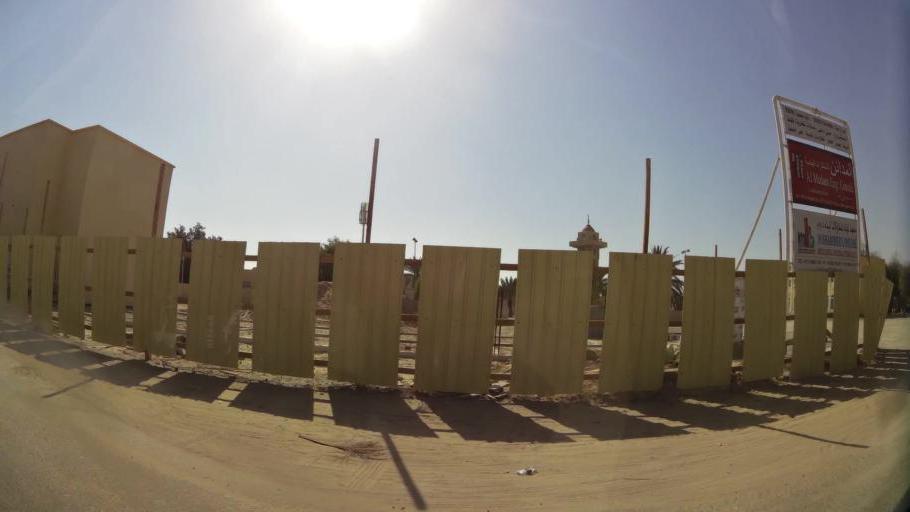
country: AE
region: Ajman
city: Ajman
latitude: 25.4094
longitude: 55.4687
